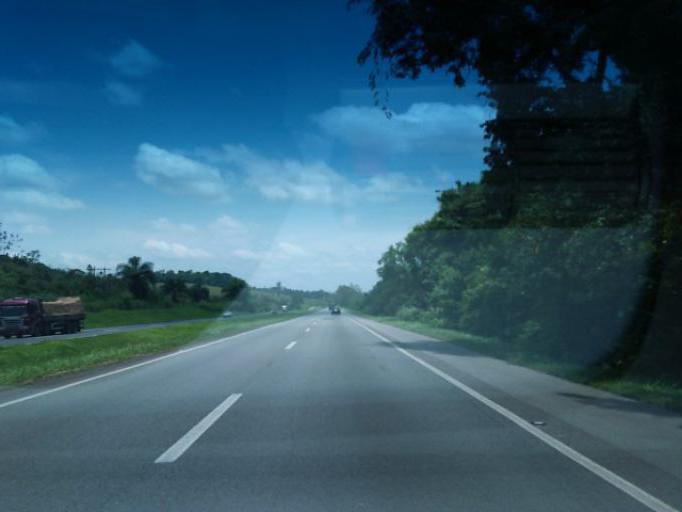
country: BR
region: Sao Paulo
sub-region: Registro
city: Registro
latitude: -24.4136
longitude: -47.7572
